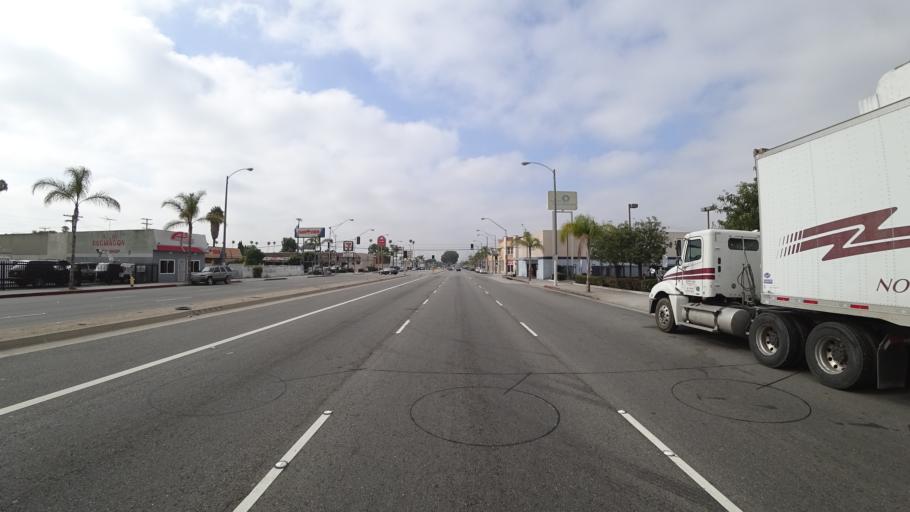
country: US
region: California
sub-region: Los Angeles County
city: Lennox
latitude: 33.9498
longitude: -118.3528
